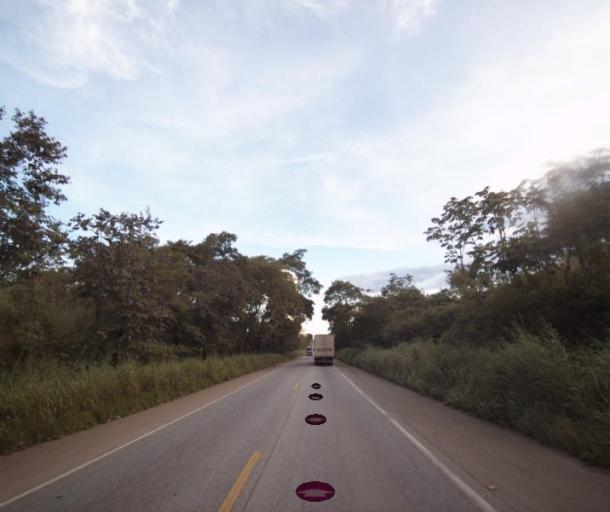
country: BR
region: Goias
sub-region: Uruacu
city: Uruacu
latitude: -14.2421
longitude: -49.1372
